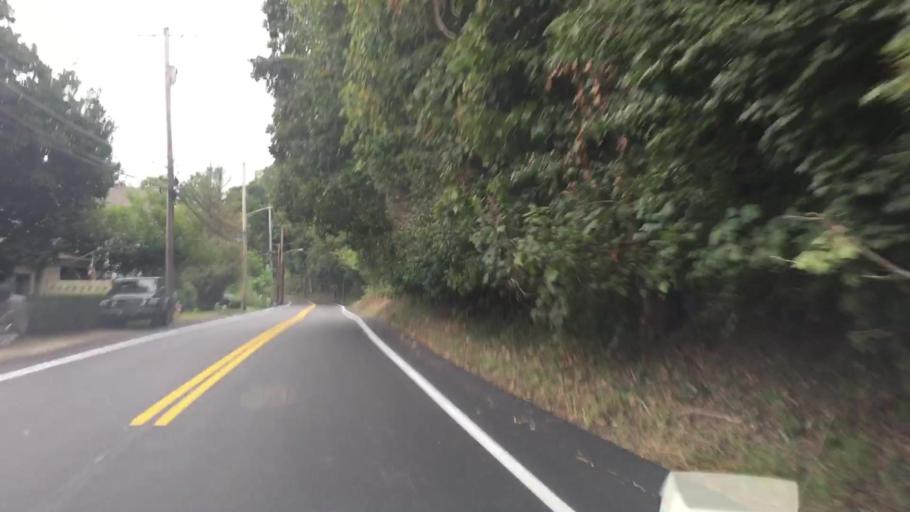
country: US
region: Pennsylvania
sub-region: Allegheny County
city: Carnegie
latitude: 40.4120
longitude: -80.0939
